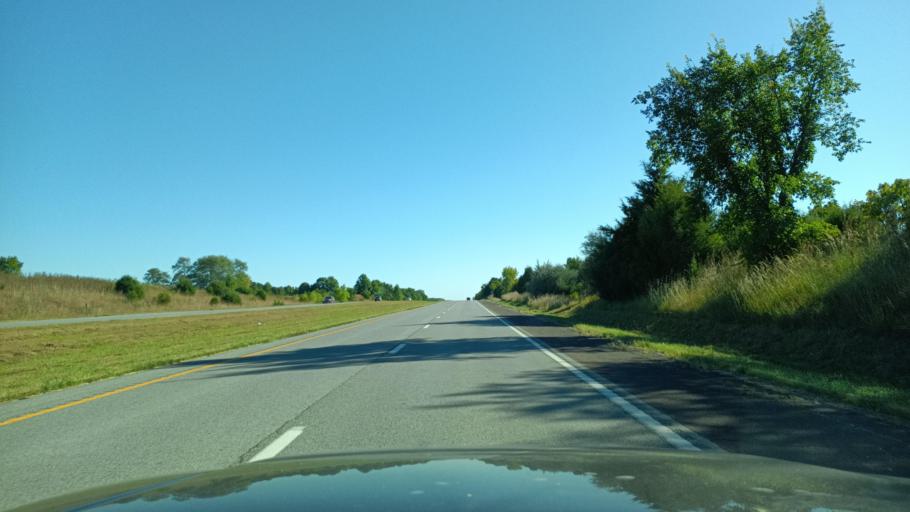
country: US
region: Missouri
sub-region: Boone County
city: Hallsville
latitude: 39.1578
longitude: -92.3311
